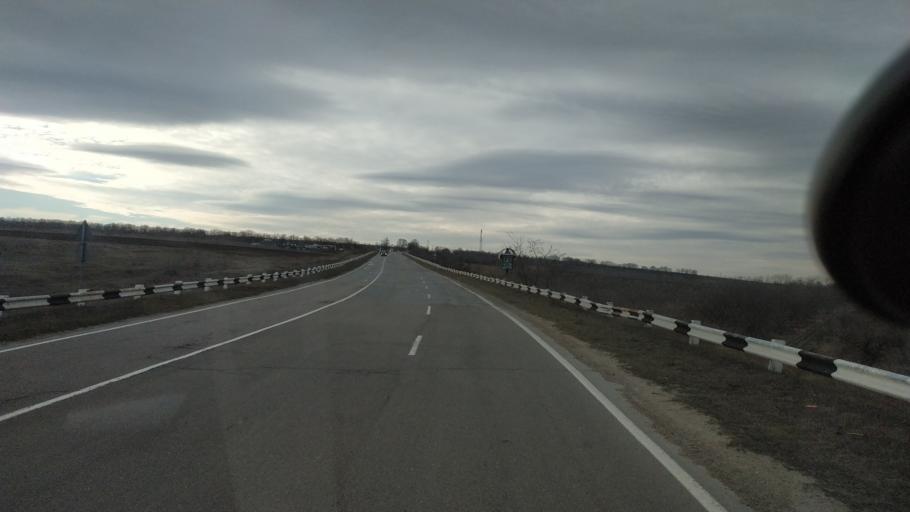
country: MD
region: Chisinau
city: Vadul lui Voda
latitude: 47.0898
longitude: 29.0664
